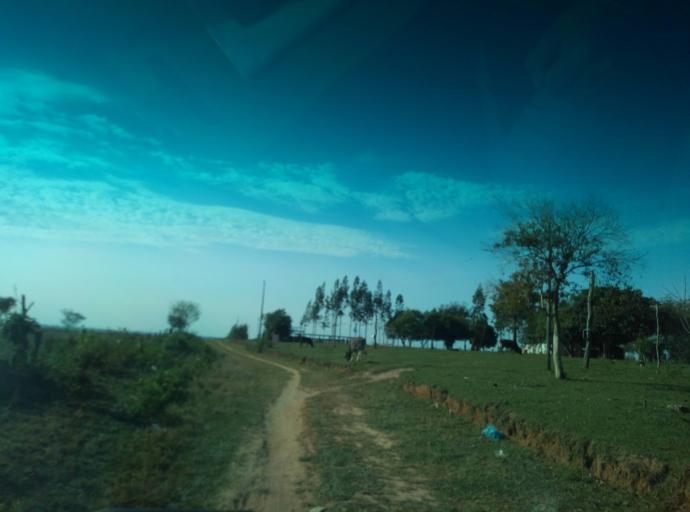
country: PY
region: Caaguazu
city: Doctor Cecilio Baez
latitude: -25.1636
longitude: -56.2321
